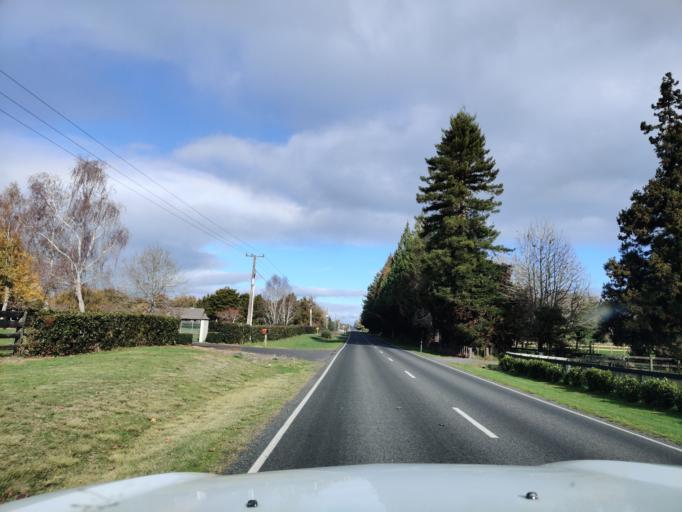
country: NZ
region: Waikato
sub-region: Waipa District
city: Cambridge
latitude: -37.8485
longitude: 175.4391
